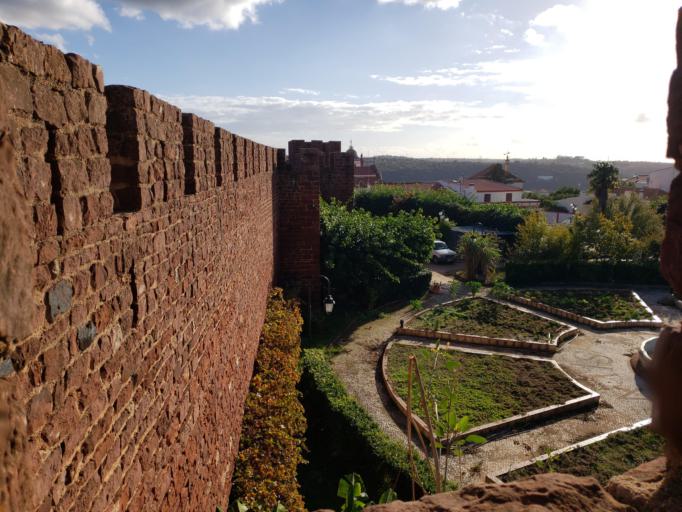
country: PT
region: Faro
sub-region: Silves
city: Silves
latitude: 37.1915
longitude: -8.4384
